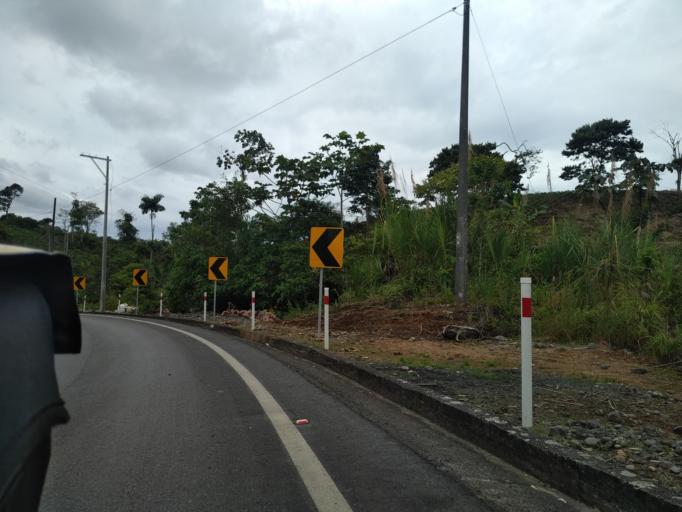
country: EC
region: Pastaza
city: Puyo
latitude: -1.3321
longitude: -77.8982
